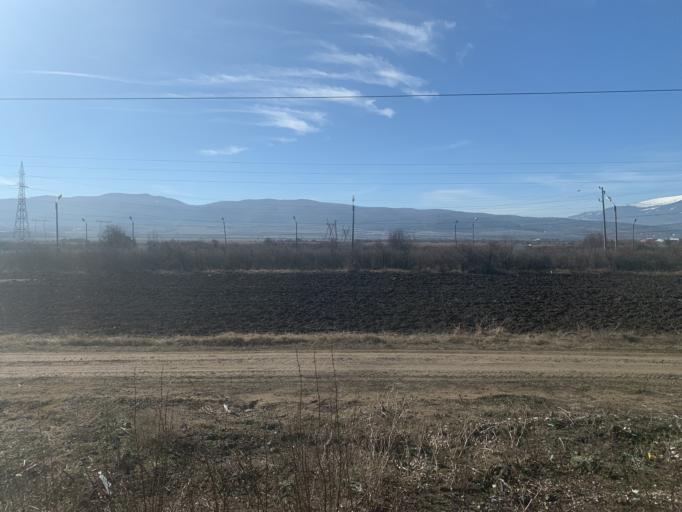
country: BG
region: Sofiya
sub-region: Obshtina Elin Pelin
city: Elin Pelin
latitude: 42.6493
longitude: 23.4834
